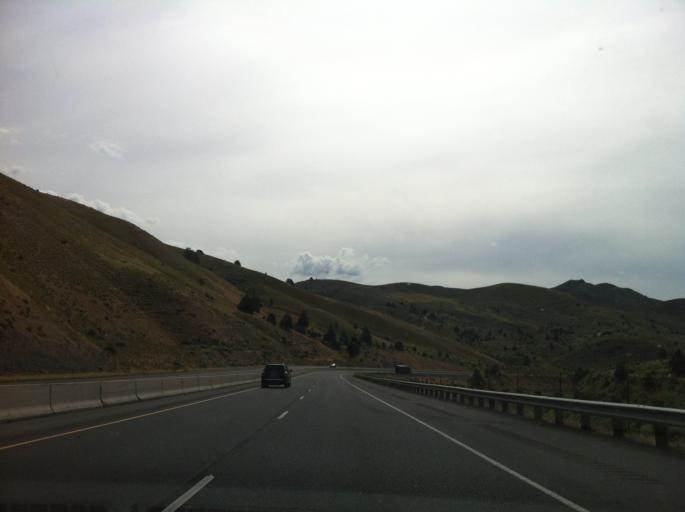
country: US
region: Idaho
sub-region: Washington County
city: Weiser
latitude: 44.5198
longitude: -117.3813
